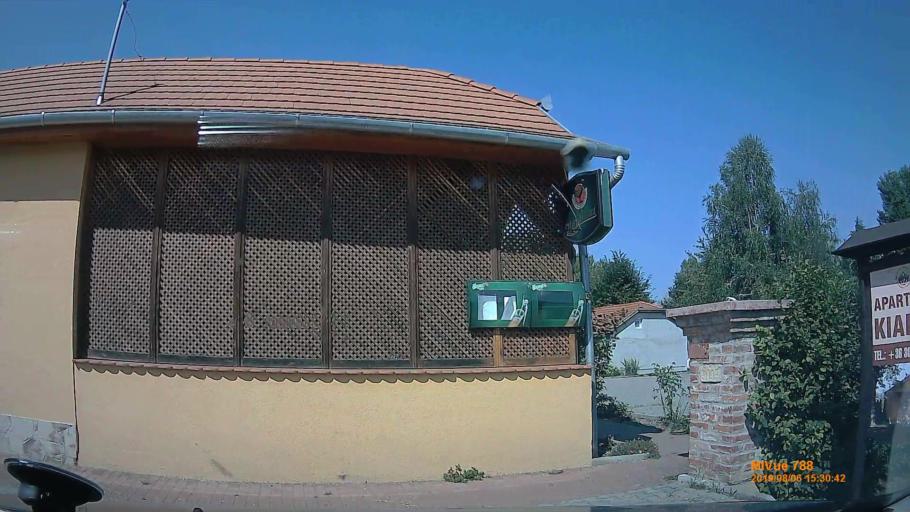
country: HR
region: Koprivnicko-Krizevacka
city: Sigetec
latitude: 46.2388
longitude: 16.9902
